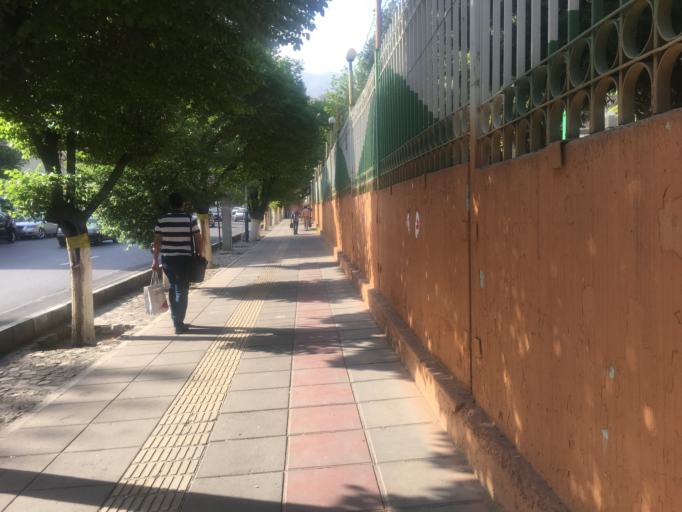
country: IR
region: Tehran
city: Tajrish
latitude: 35.7926
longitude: 51.4773
